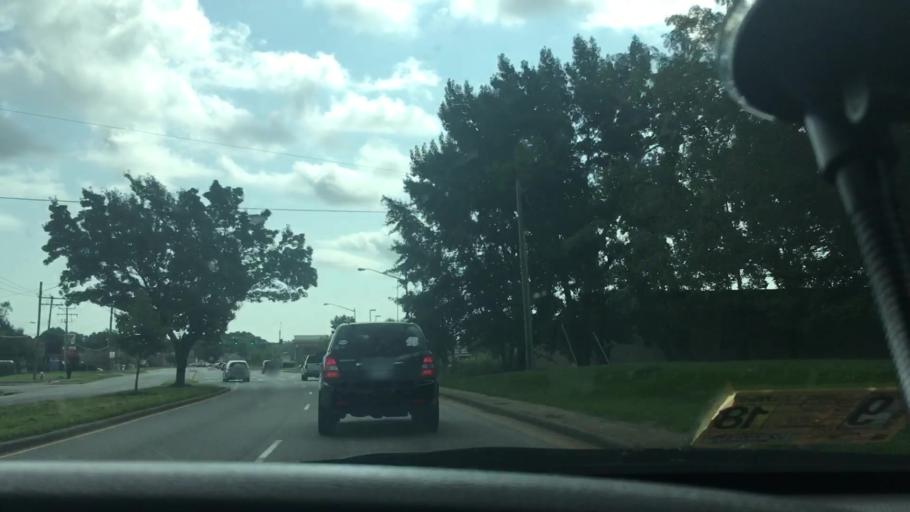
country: US
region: Virginia
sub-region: City of Virginia Beach
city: Virginia Beach
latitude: 36.8161
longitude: -76.1139
